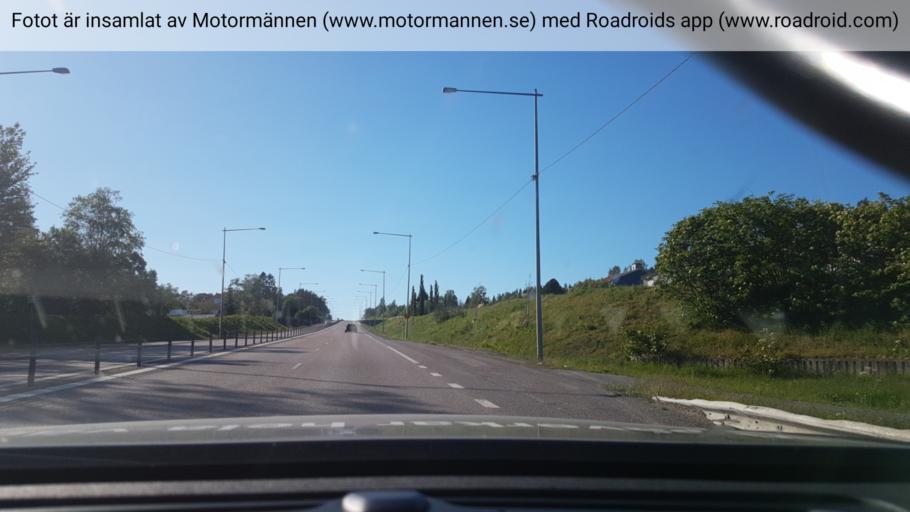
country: SE
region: Vaesternorrland
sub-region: Haernoesands Kommun
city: Haernoesand
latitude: 62.6444
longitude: 17.9076
